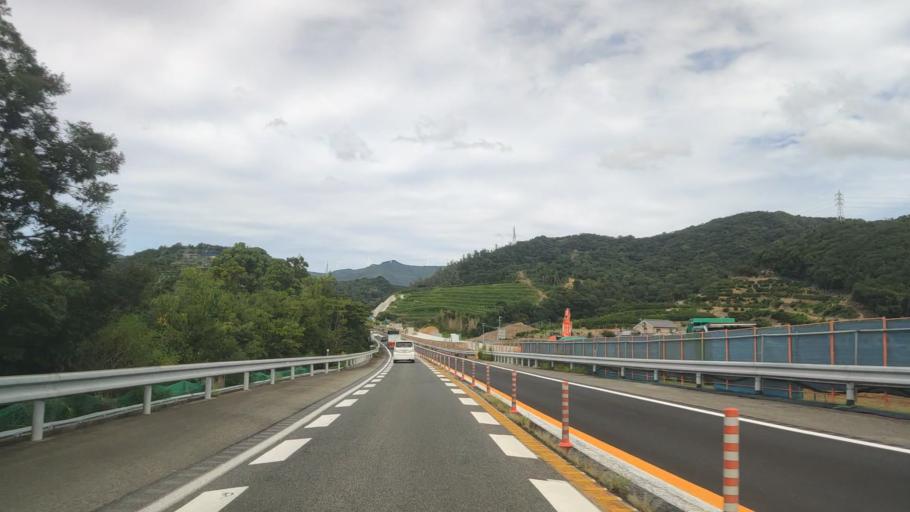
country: JP
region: Wakayama
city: Gobo
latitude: 33.9134
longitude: 135.1944
